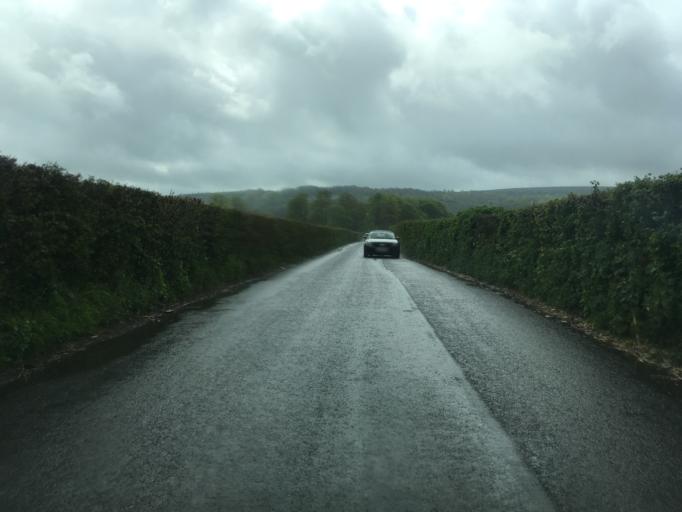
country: GB
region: England
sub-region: North Somerset
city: Burrington
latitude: 51.3383
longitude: -2.7451
